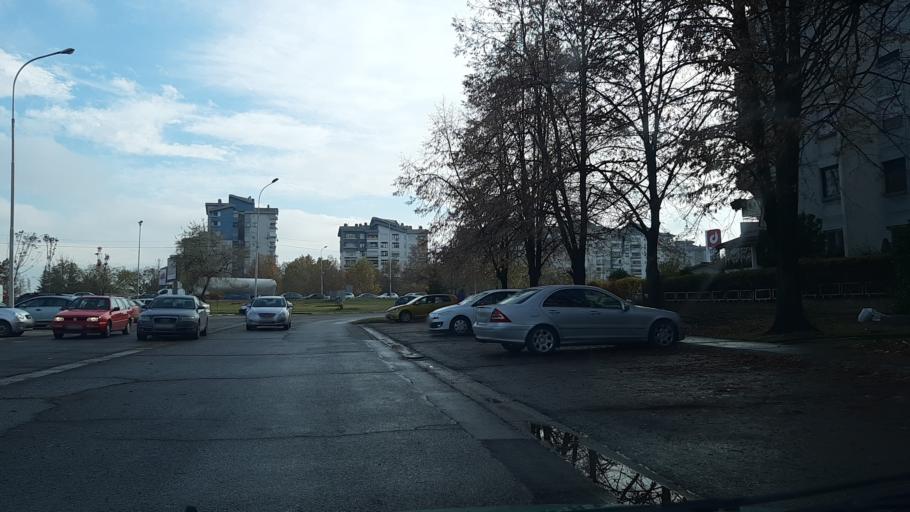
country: MK
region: Kisela Voda
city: Usje
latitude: 41.9894
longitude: 21.4728
